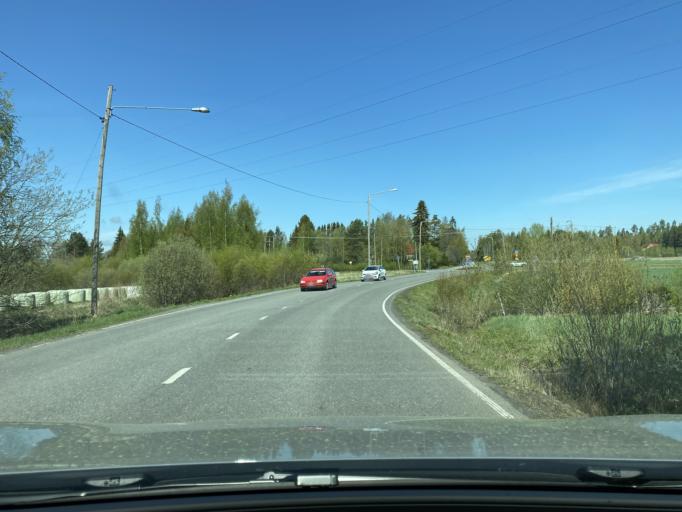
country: FI
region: Pirkanmaa
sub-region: Lounais-Pirkanmaa
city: Vammala
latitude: 61.3517
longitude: 22.8705
